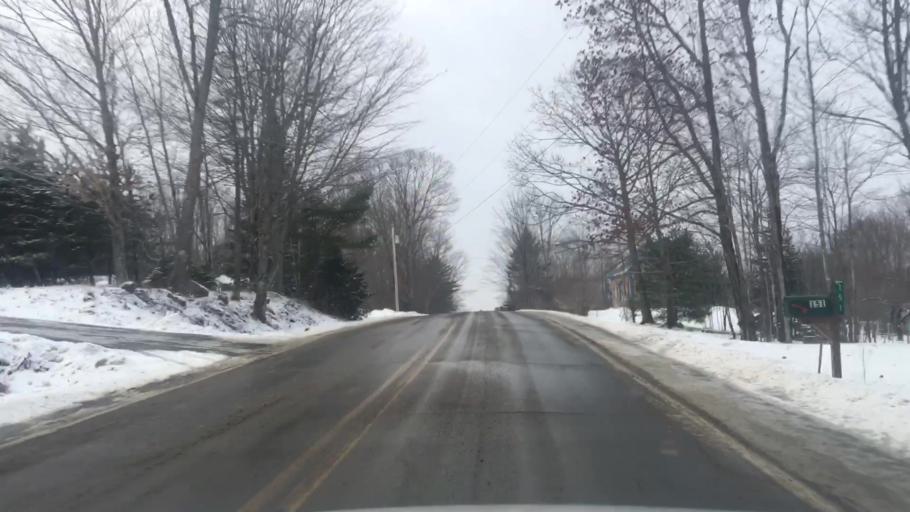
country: US
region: Maine
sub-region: Waldo County
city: Searsmont
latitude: 44.3612
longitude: -69.1672
